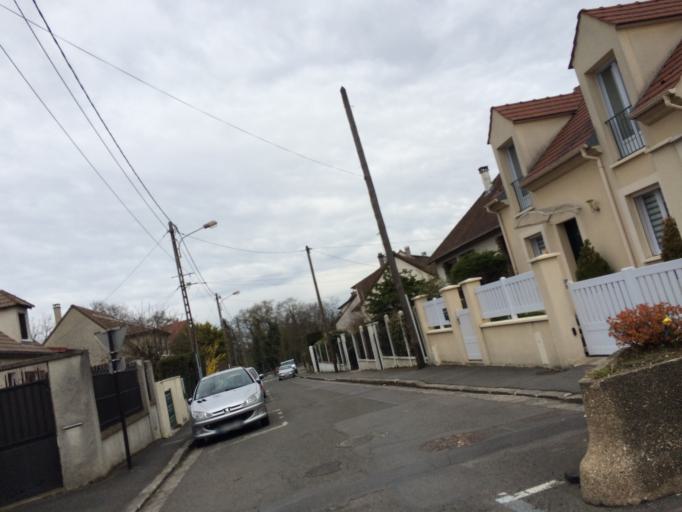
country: FR
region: Ile-de-France
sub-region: Departement de l'Essonne
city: Palaiseau
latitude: 48.7301
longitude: 2.2528
